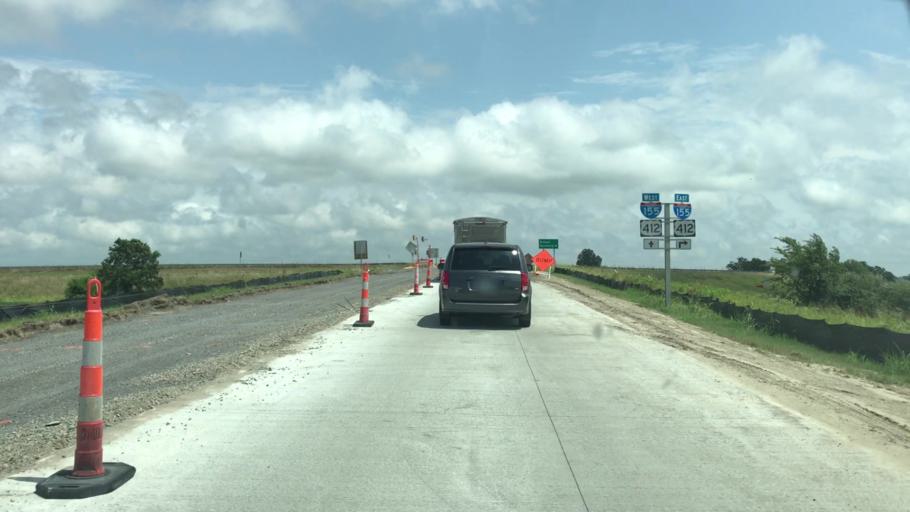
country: US
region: Missouri
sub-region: Pemiscot County
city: Caruthersville
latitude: 36.1762
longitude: -89.6967
